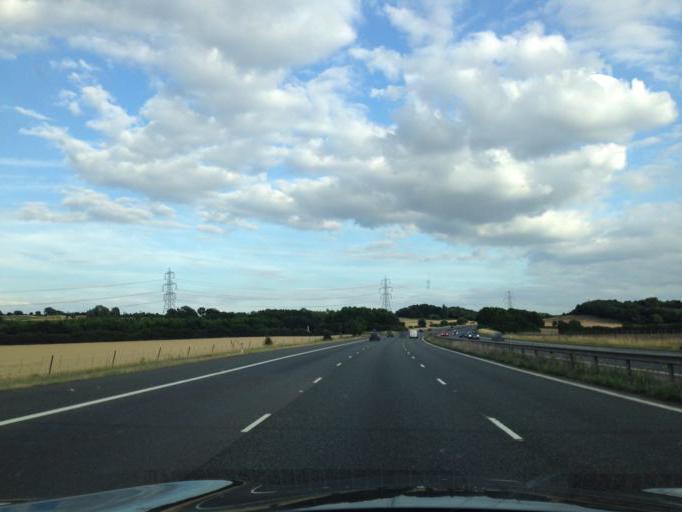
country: GB
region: England
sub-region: Oxfordshire
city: Bicester
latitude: 51.8295
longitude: -1.1158
